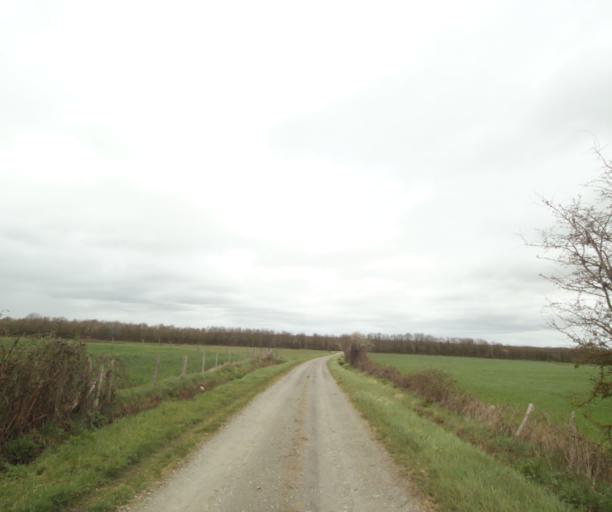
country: FR
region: Pays de la Loire
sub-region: Departement de la Loire-Atlantique
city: Bouvron
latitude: 47.4237
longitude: -1.8458
